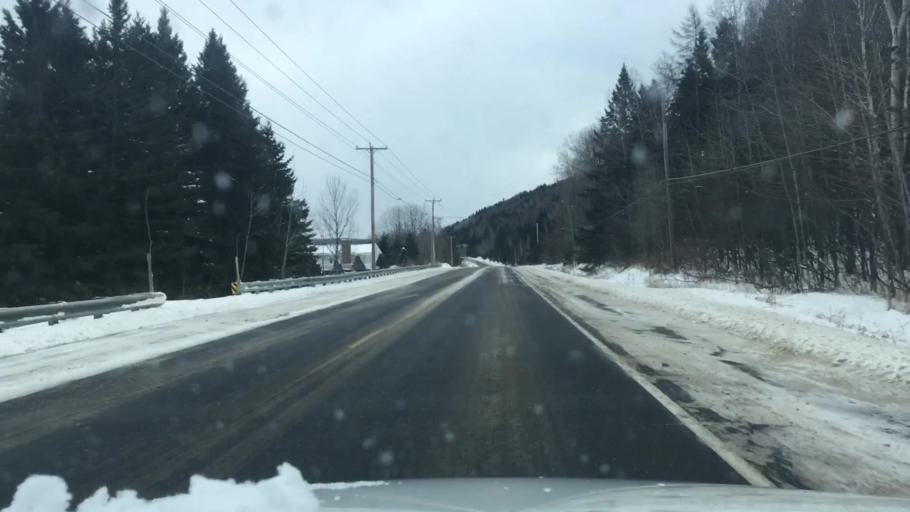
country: US
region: Maine
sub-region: Aroostook County
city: Madawaska
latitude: 47.3321
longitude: -68.2048
